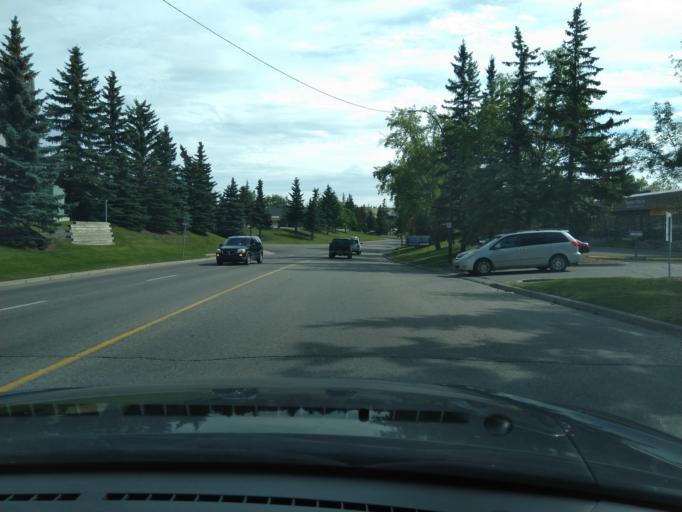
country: CA
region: Alberta
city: Calgary
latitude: 51.0799
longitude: -114.0269
